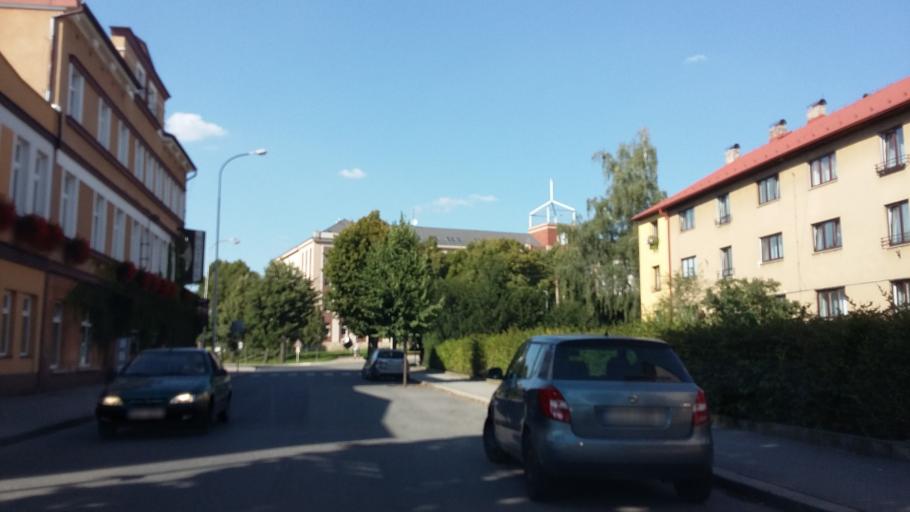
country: CZ
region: Liberecky
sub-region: Okres Semily
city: Turnov
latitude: 50.5925
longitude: 15.1622
